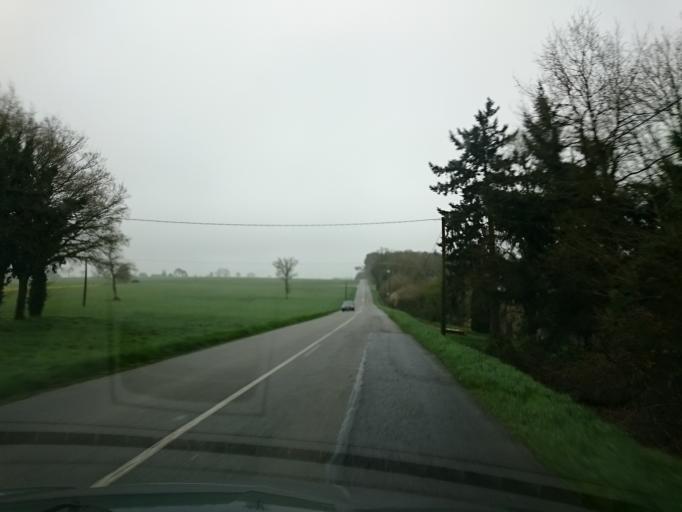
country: FR
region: Brittany
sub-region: Departement d'Ille-et-Vilaine
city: Bourg-des-Comptes
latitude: 47.9236
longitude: -1.7102
